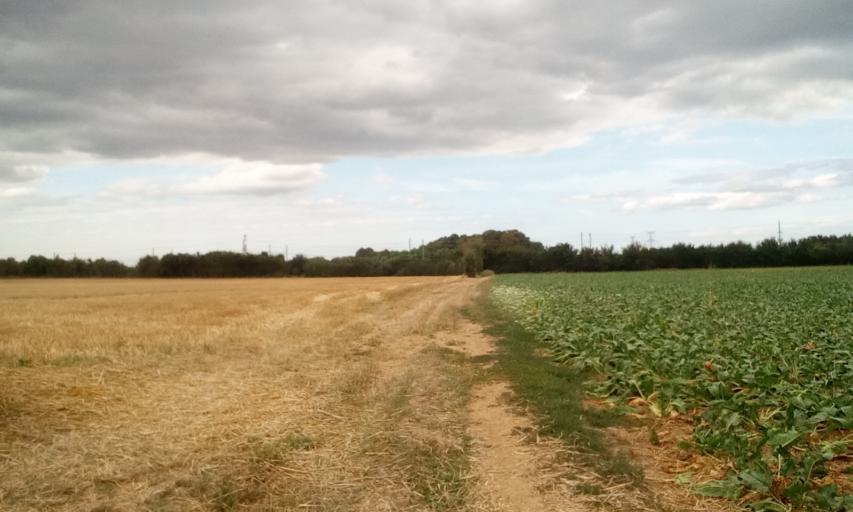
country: FR
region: Lower Normandy
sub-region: Departement du Calvados
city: Bellengreville
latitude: 49.1240
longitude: -0.2235
